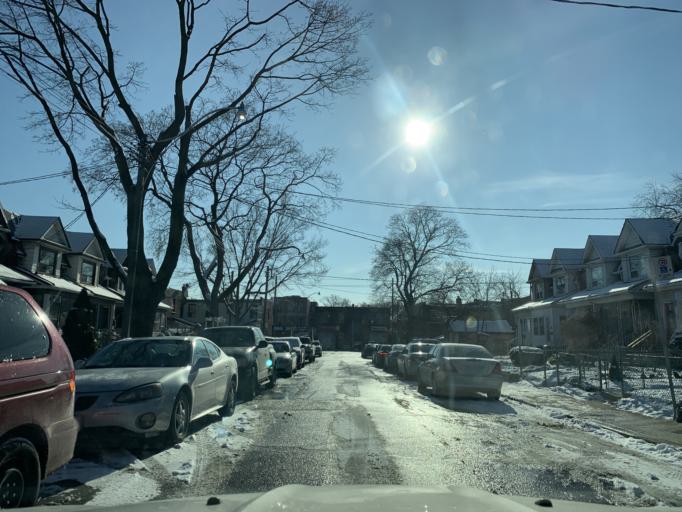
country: CA
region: Ontario
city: Toronto
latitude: 43.6704
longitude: -79.4811
